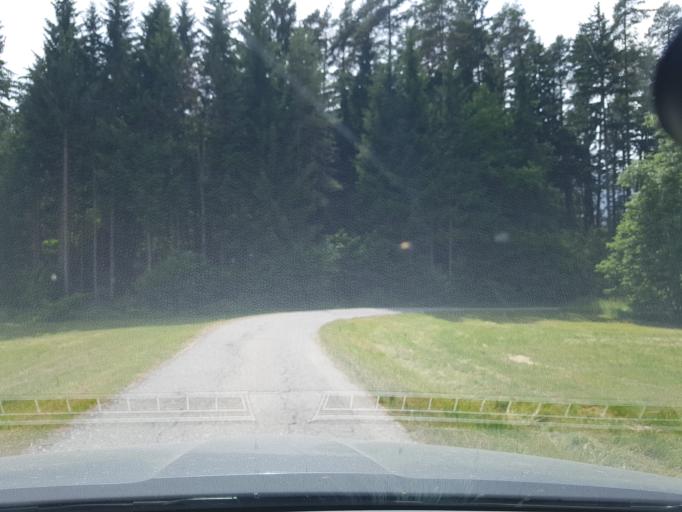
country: AT
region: Carinthia
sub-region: Politischer Bezirk Spittal an der Drau
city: Millstatt
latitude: 46.7802
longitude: 13.5554
